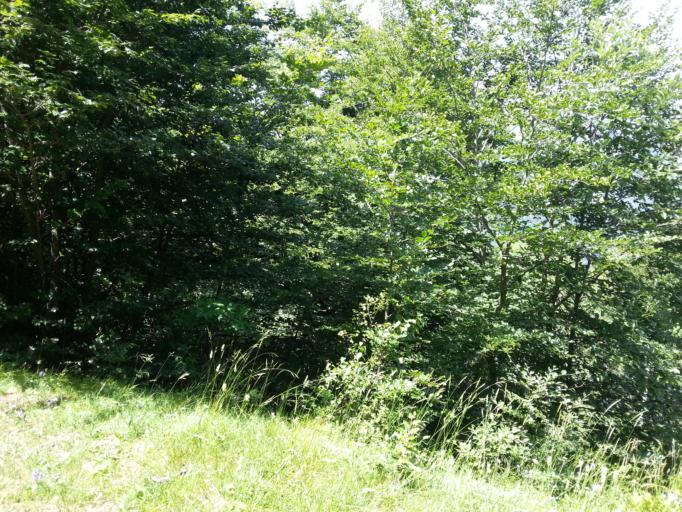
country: IT
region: Lombardy
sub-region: Provincia di Lecco
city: Cremeno
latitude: 45.9130
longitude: 9.4493
